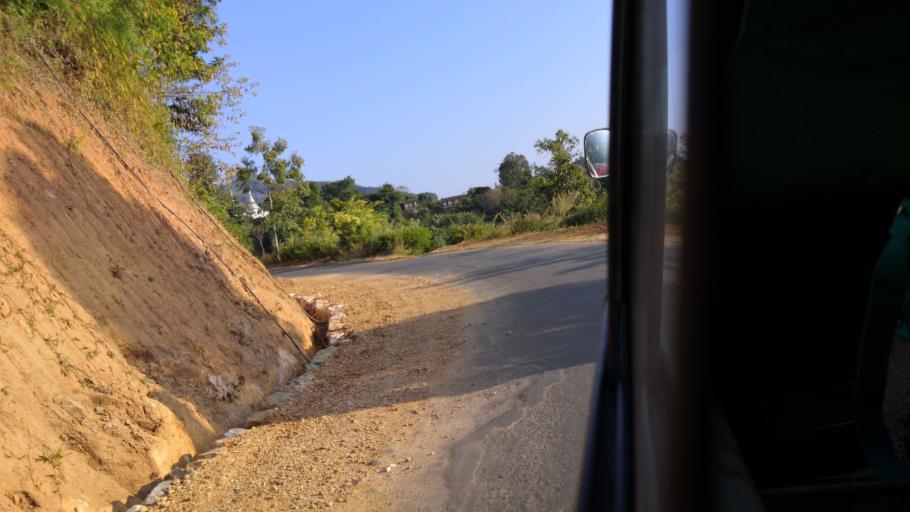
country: MM
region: Mandalay
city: Mogok
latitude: 22.9047
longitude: 96.3879
